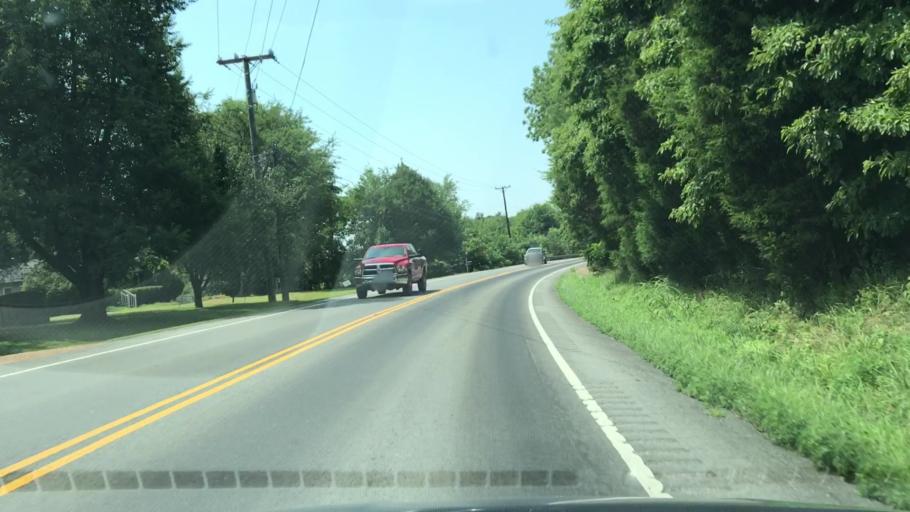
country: US
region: Tennessee
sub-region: Wilson County
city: Rural Hill
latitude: 36.1006
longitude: -86.5520
